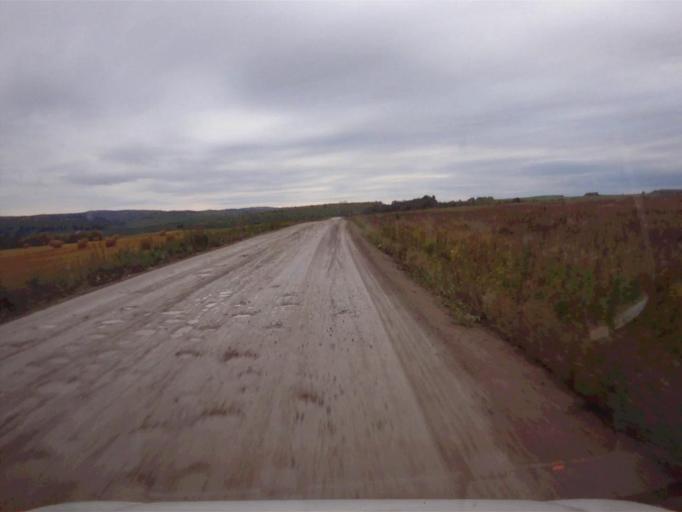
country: RU
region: Sverdlovsk
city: Mikhaylovsk
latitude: 56.1811
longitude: 59.1889
